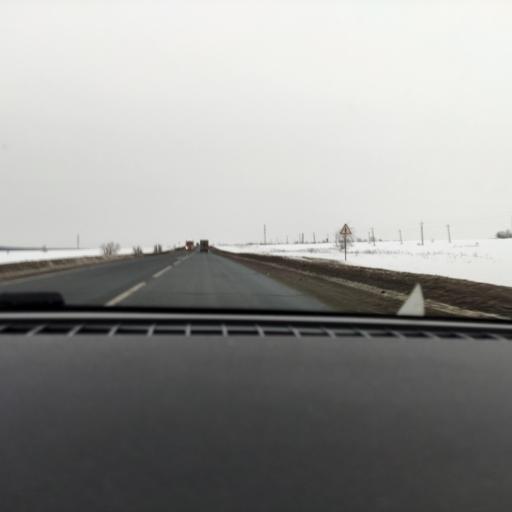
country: RU
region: Samara
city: Smyshlyayevka
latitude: 53.2920
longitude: 50.4602
